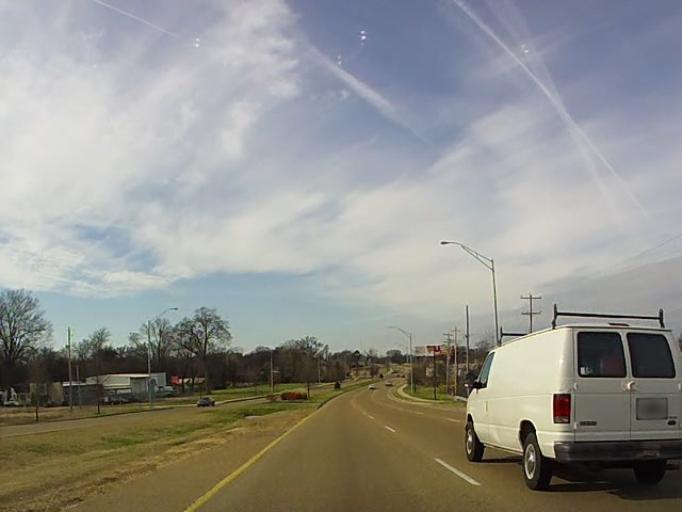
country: US
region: Tennessee
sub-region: Shelby County
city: Memphis
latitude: 35.1471
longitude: -89.9570
